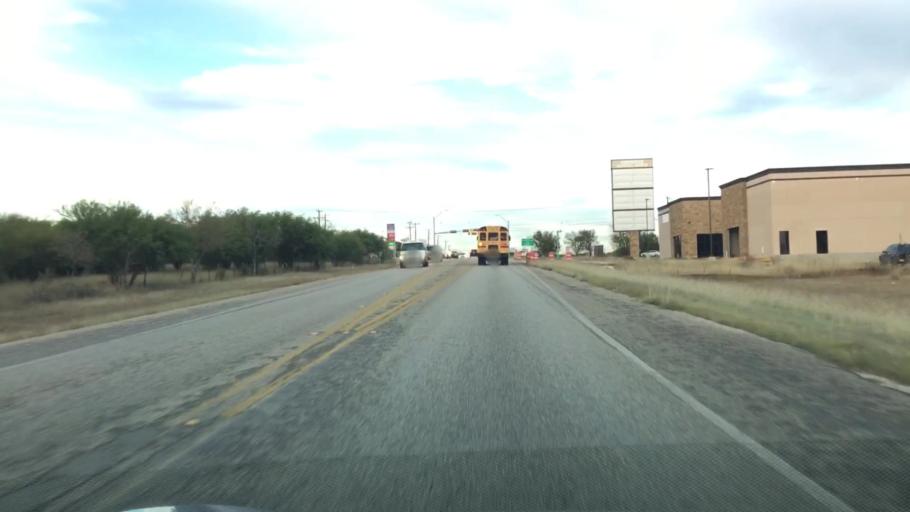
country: US
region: Texas
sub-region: Bexar County
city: Converse
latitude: 29.5258
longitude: -98.3101
